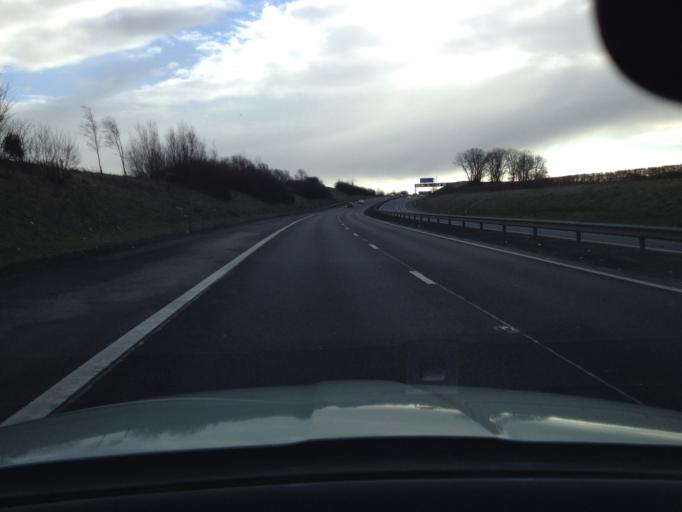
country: GB
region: Scotland
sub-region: Edinburgh
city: Kirkliston
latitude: 55.9679
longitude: -3.3907
